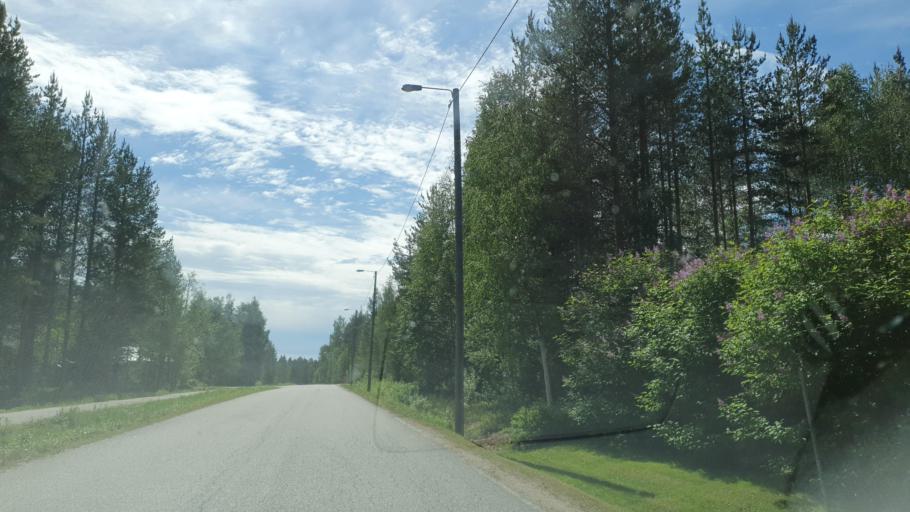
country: FI
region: Kainuu
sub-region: Kehys-Kainuu
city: Hyrynsalmi
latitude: 64.6906
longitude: 28.4705
